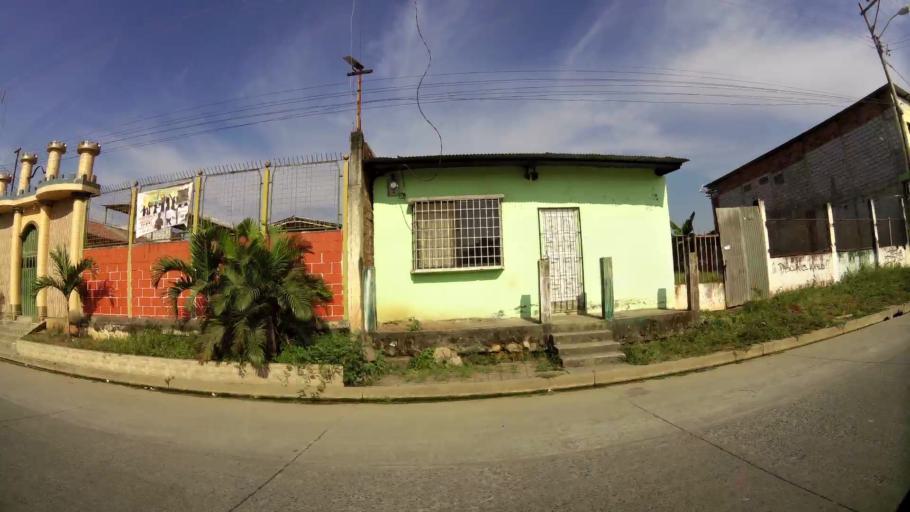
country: EC
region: Guayas
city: Eloy Alfaro
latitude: -2.0691
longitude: -79.9285
